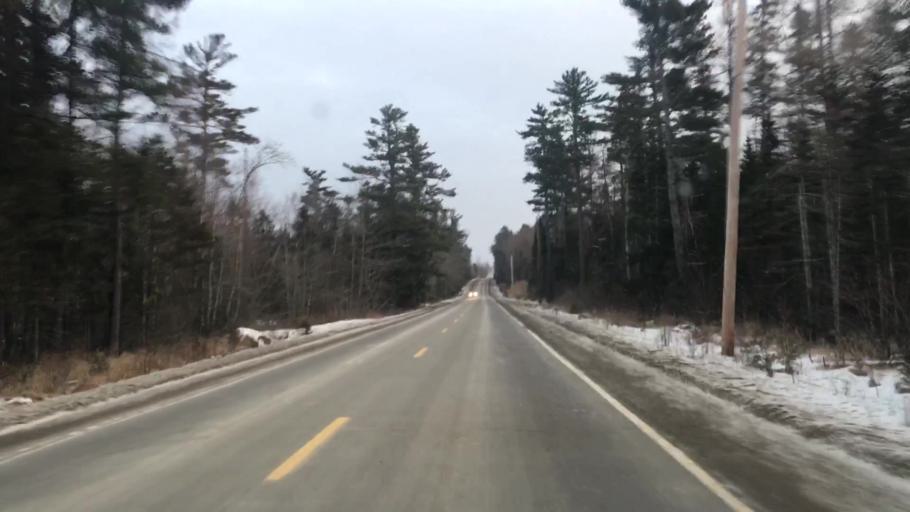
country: US
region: Maine
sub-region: Hancock County
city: Ellsworth
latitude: 44.6780
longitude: -68.3527
